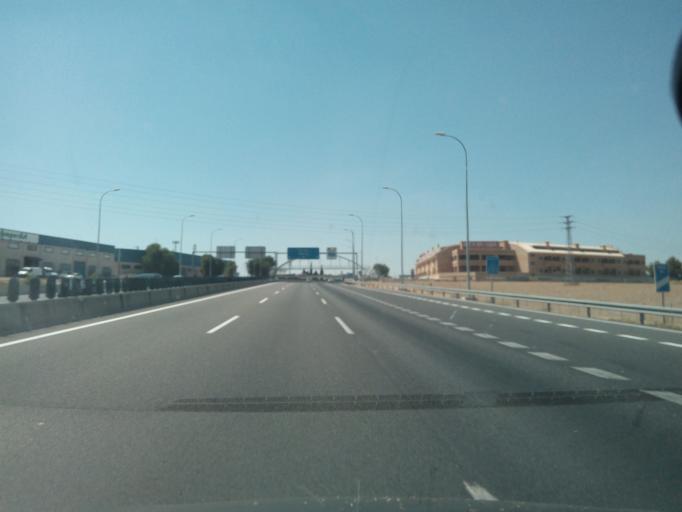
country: ES
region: Castille-La Mancha
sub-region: Province of Toledo
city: Sesena
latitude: 40.1029
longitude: -3.6414
